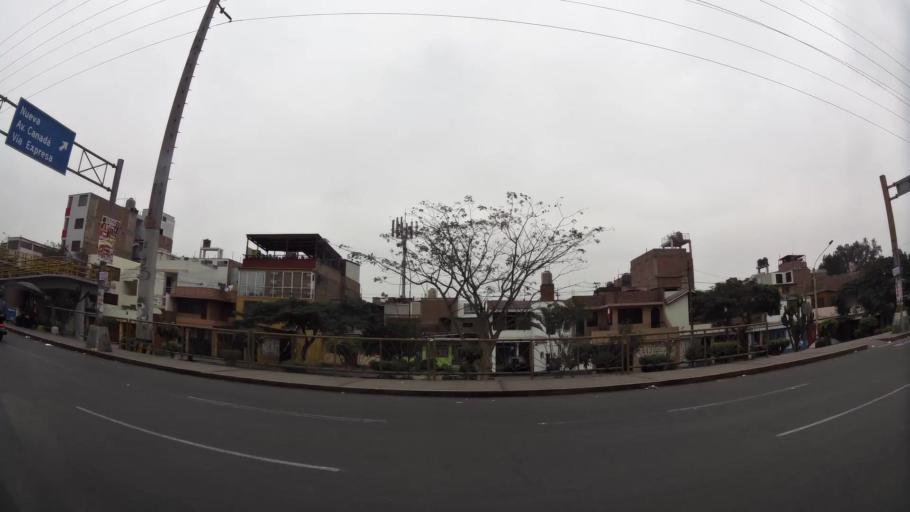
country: PE
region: Lima
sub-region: Lima
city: San Luis
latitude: -12.0769
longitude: -76.9895
